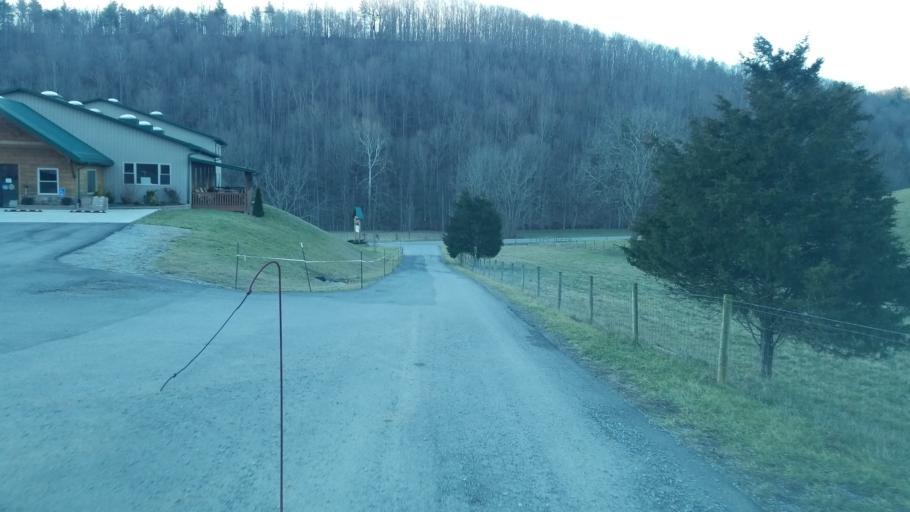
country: US
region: Virginia
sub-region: Giles County
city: Narrows
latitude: 37.1904
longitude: -80.8463
